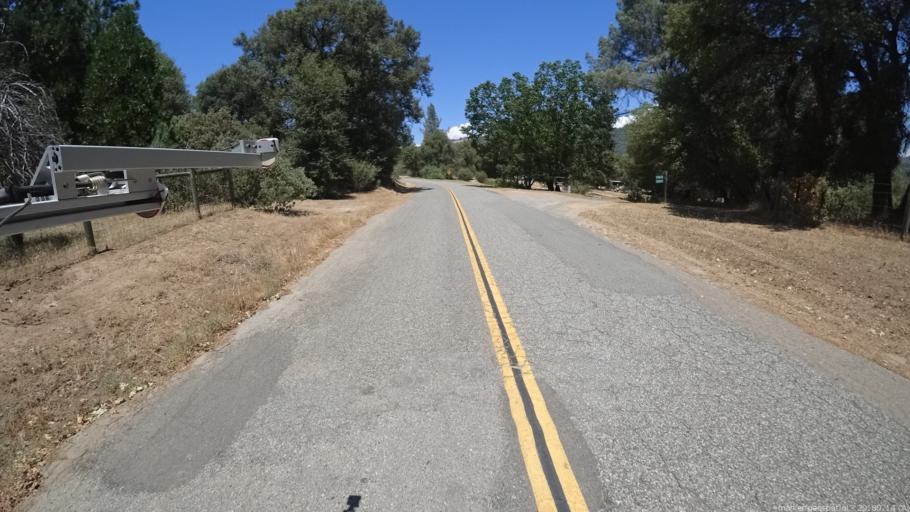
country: US
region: California
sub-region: Madera County
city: Ahwahnee
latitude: 37.4081
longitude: -119.7237
